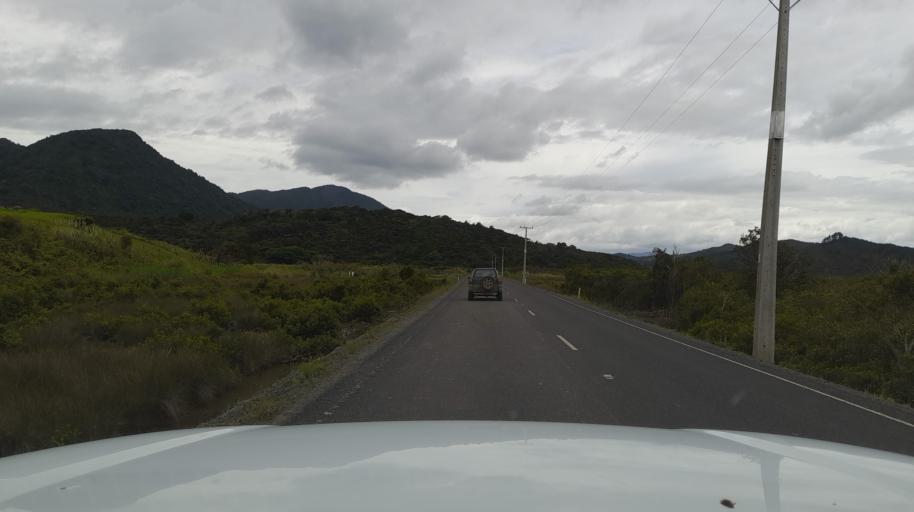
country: NZ
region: Northland
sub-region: Far North District
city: Kaitaia
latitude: -35.4057
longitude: 173.3823
